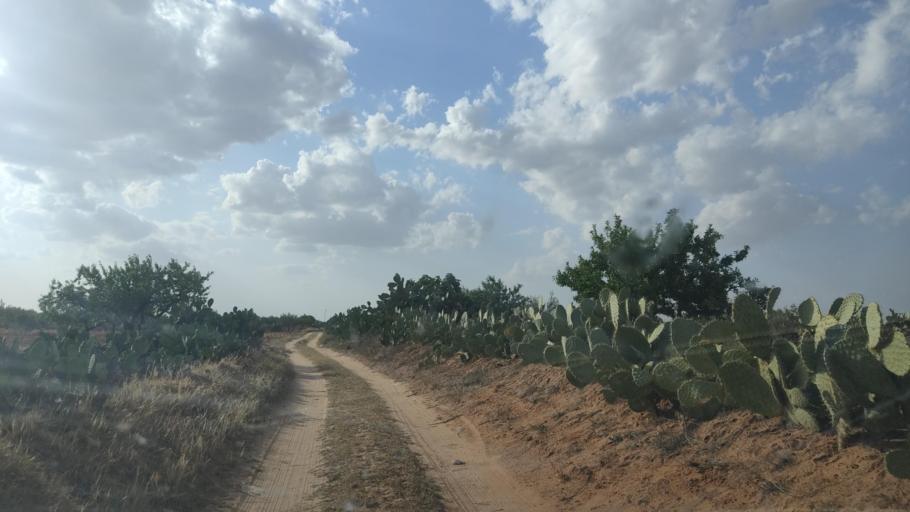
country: TN
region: Safaqis
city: Sfax
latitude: 34.8527
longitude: 10.5927
